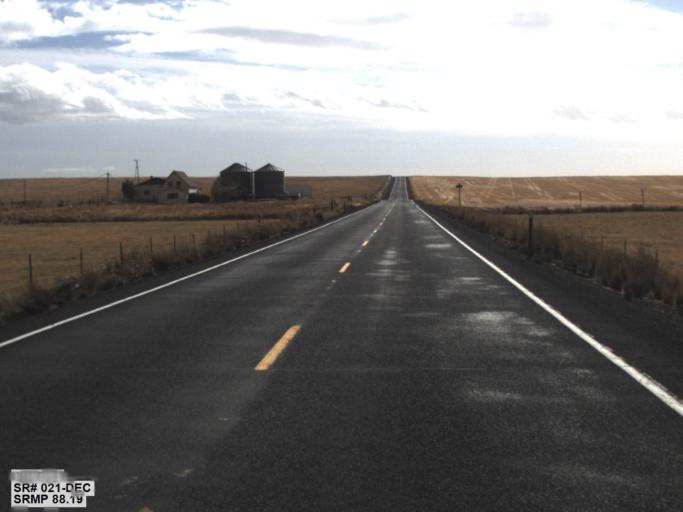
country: US
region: Washington
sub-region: Okanogan County
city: Coulee Dam
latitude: 47.7152
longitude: -118.7221
